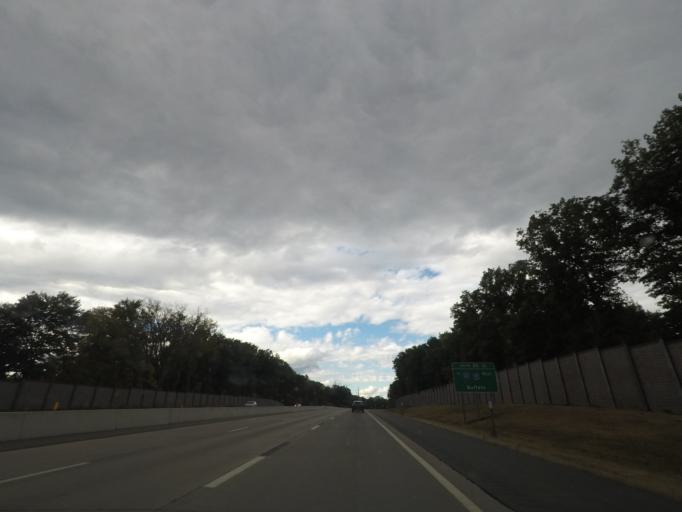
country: US
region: New York
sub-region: Albany County
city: McKownville
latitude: 42.6726
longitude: -73.8408
